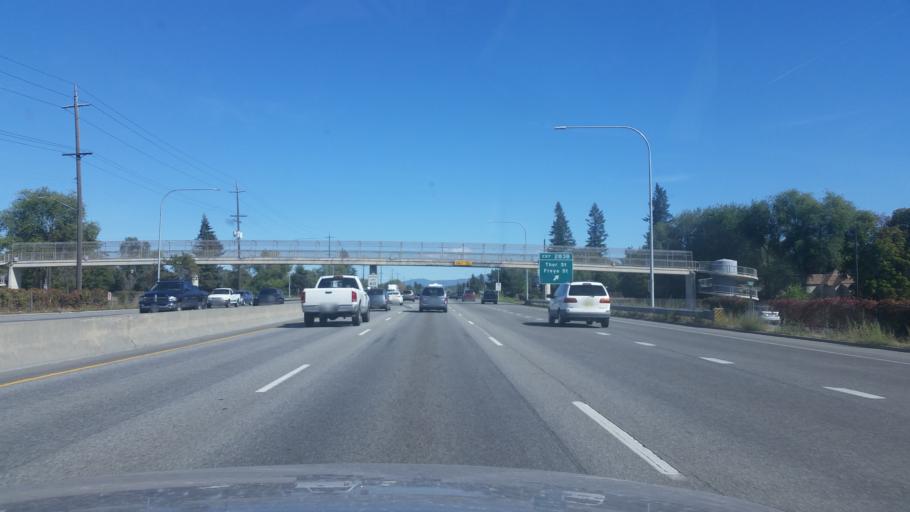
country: US
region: Washington
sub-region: Spokane County
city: Spokane
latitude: 47.6540
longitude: -117.3693
